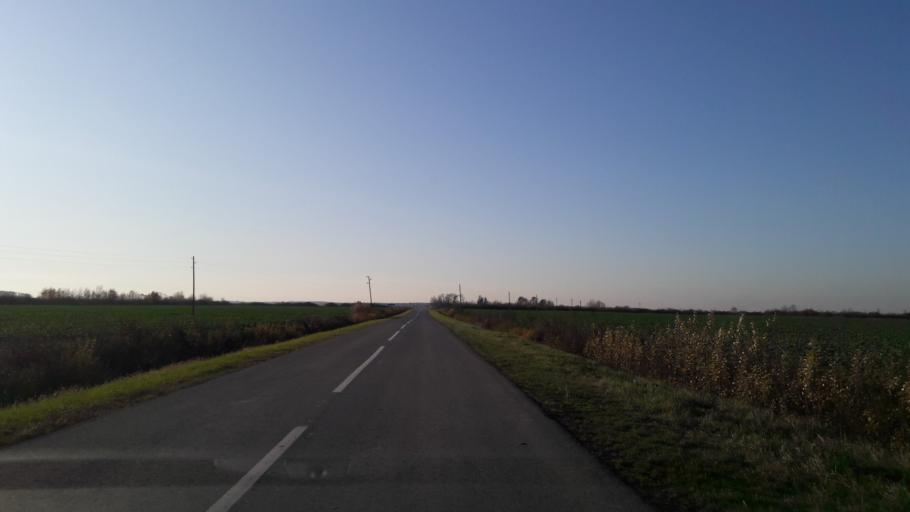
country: HR
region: Osjecko-Baranjska
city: Vuka
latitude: 45.4213
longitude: 18.5327
